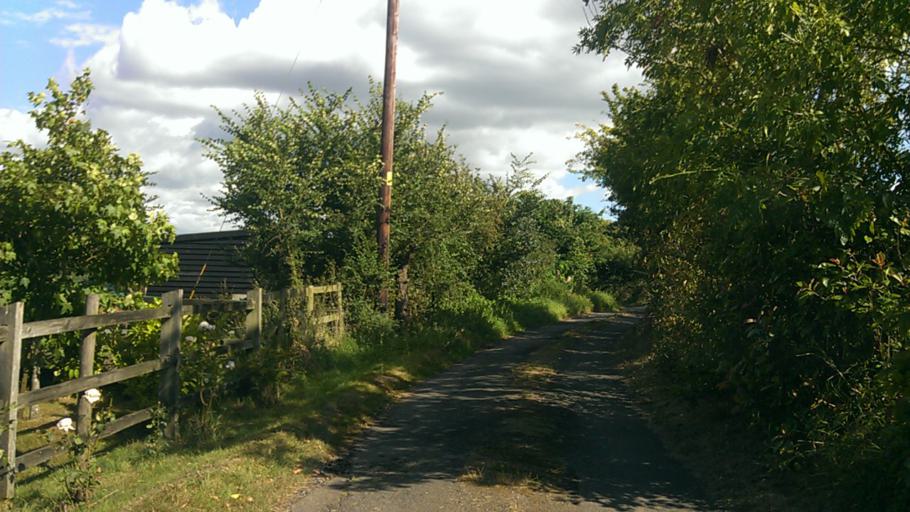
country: GB
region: England
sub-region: Essex
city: Layer de la Haye
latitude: 51.8366
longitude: 0.9009
